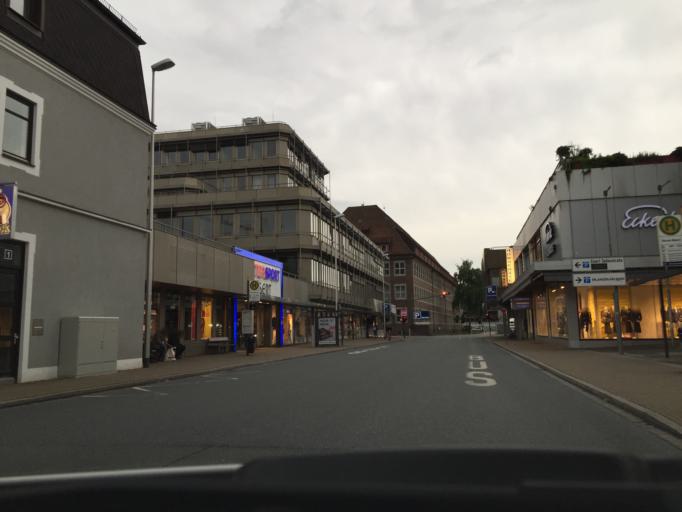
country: DE
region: Bavaria
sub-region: Regierungsbezirk Mittelfranken
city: Erlangen
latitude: 49.5911
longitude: 11.0060
